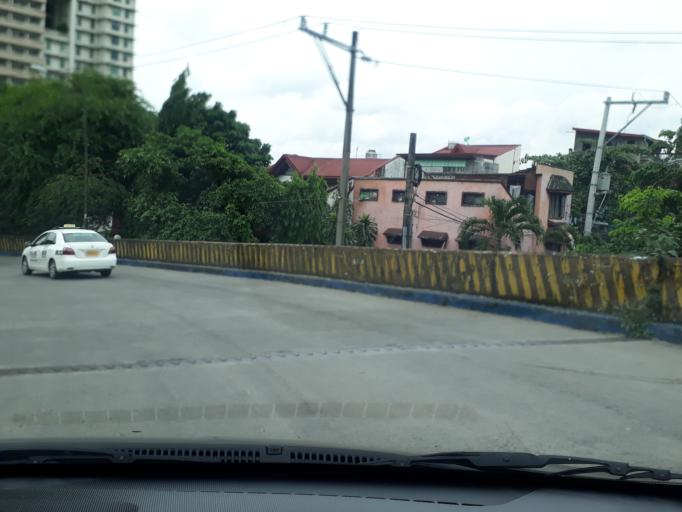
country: PH
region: Metro Manila
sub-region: Mandaluyong
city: Mandaluyong City
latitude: 14.5699
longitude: 121.0322
